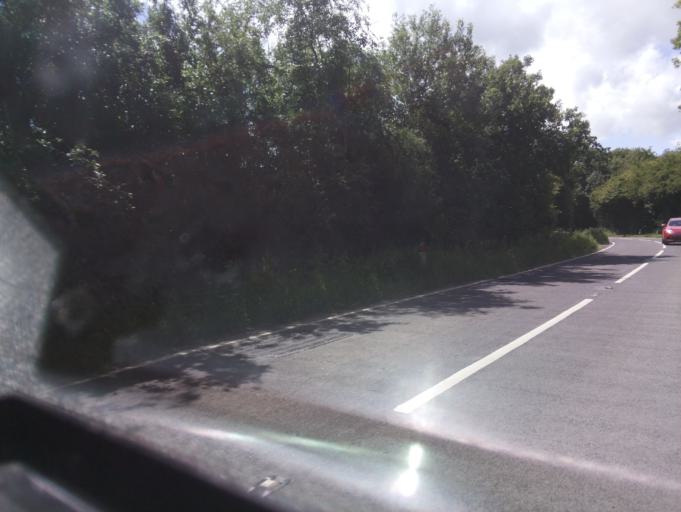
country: GB
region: England
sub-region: Nottinghamshire
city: Burton Joyce
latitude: 53.0034
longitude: -1.0486
